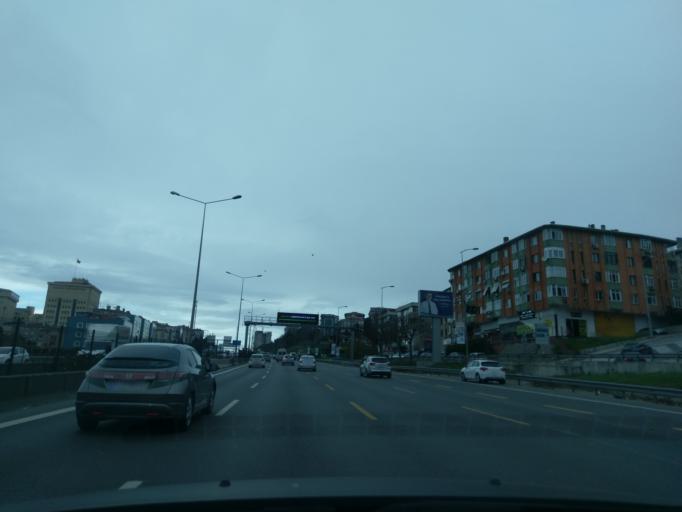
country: TR
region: Istanbul
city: UEskuedar
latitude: 41.0004
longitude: 29.0524
